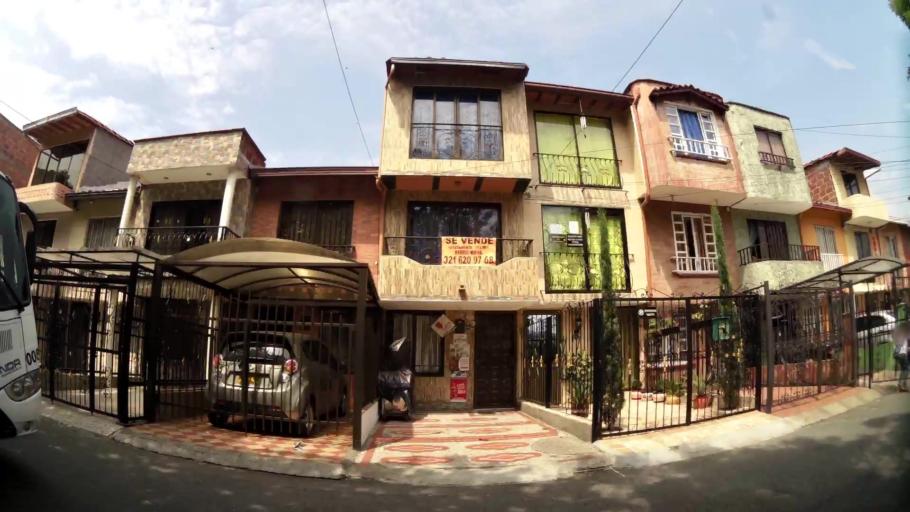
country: CO
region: Antioquia
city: Bello
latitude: 6.3192
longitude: -75.5594
